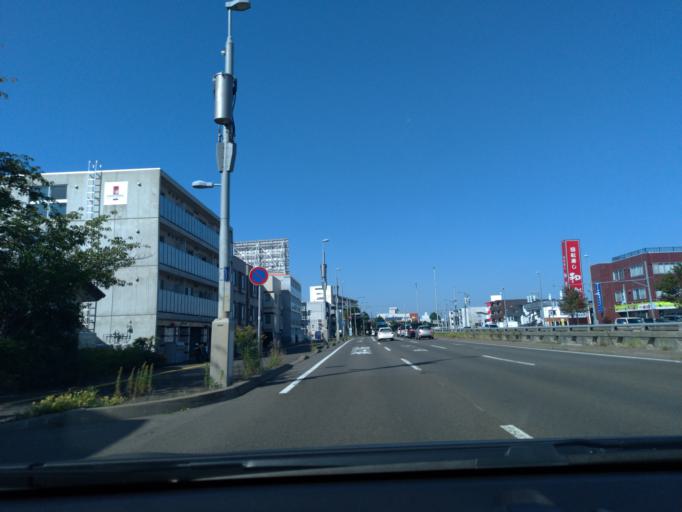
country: JP
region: Hokkaido
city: Sapporo
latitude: 43.1088
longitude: 141.3437
